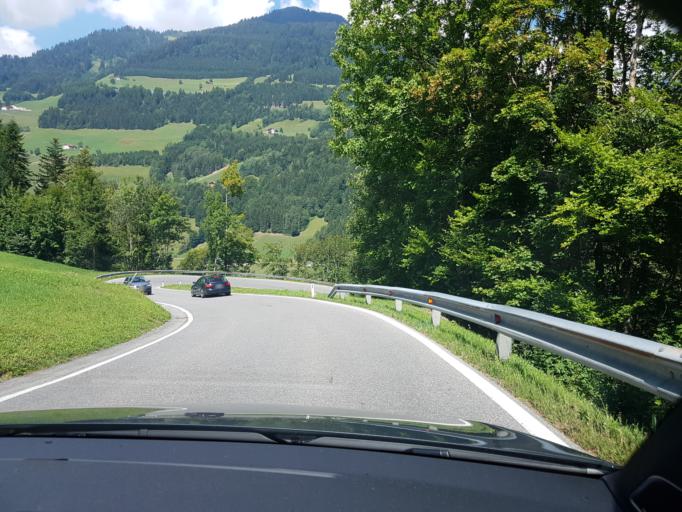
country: AT
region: Vorarlberg
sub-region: Politischer Bezirk Bludenz
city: Raggal
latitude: 47.2180
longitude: 9.8580
